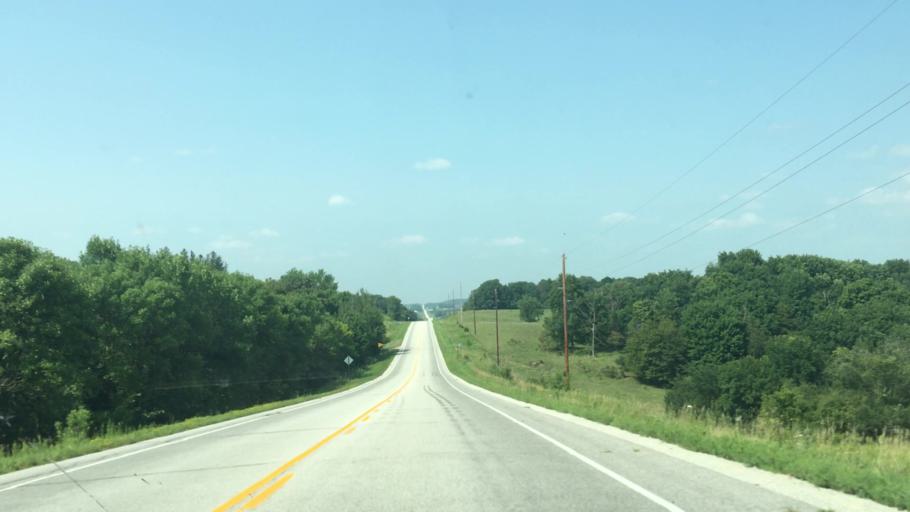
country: US
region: Minnesota
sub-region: Fillmore County
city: Harmony
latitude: 43.5815
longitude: -91.9299
